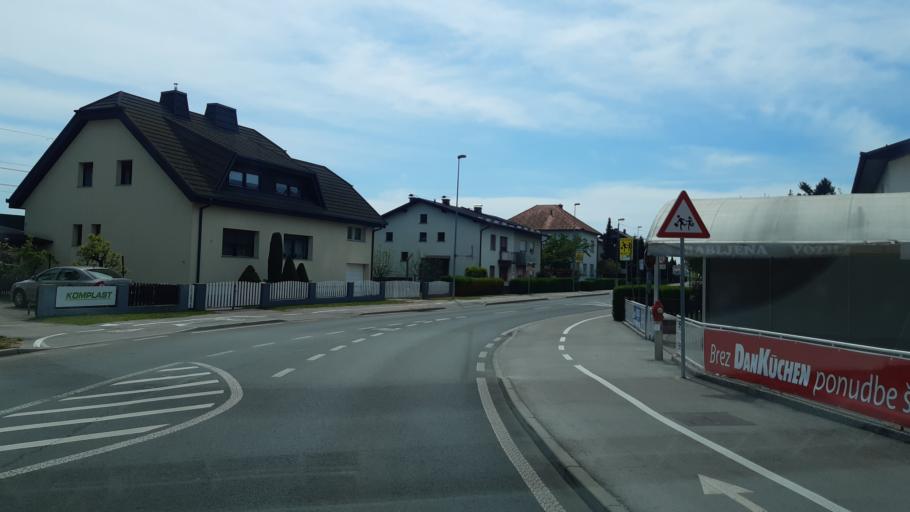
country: SI
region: Murska Sobota
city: Murska Sobota
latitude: 46.6556
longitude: 16.1699
